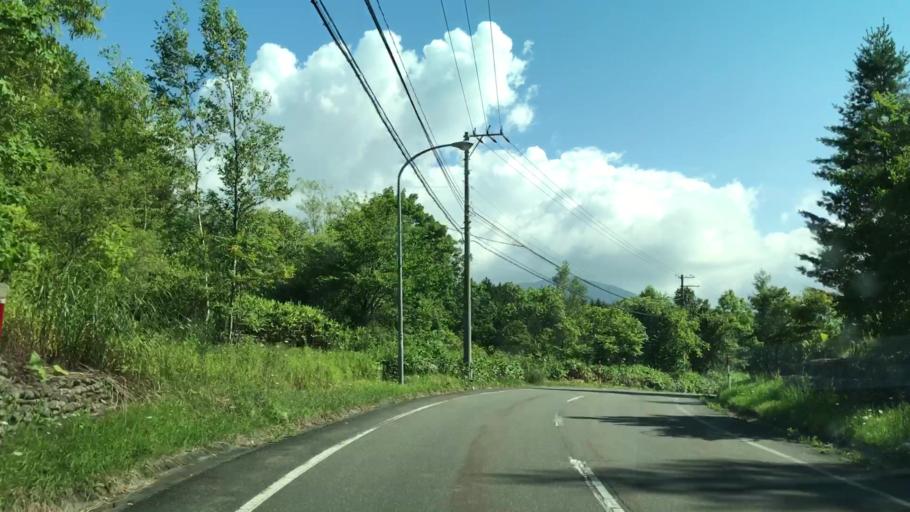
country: JP
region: Hokkaido
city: Shimo-furano
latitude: 42.8601
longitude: 142.4406
